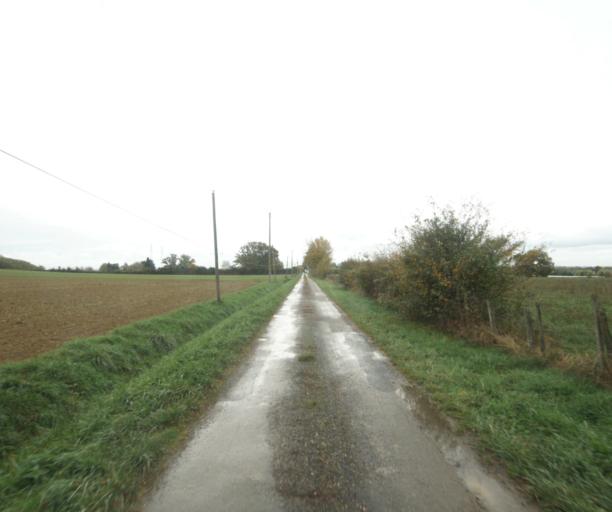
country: FR
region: Rhone-Alpes
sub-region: Departement de l'Ain
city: Pont-de-Vaux
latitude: 46.4847
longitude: 4.8818
